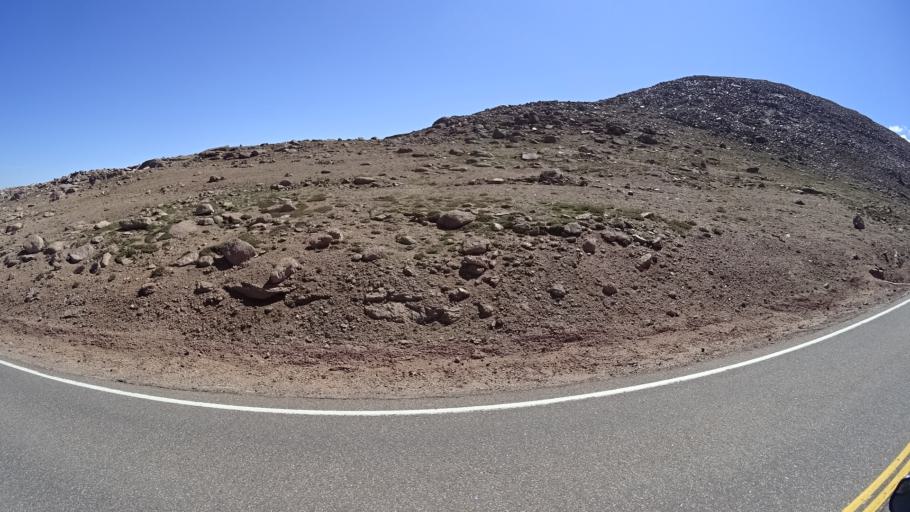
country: US
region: Colorado
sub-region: El Paso County
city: Cascade-Chipita Park
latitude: 38.8448
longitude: -105.0510
